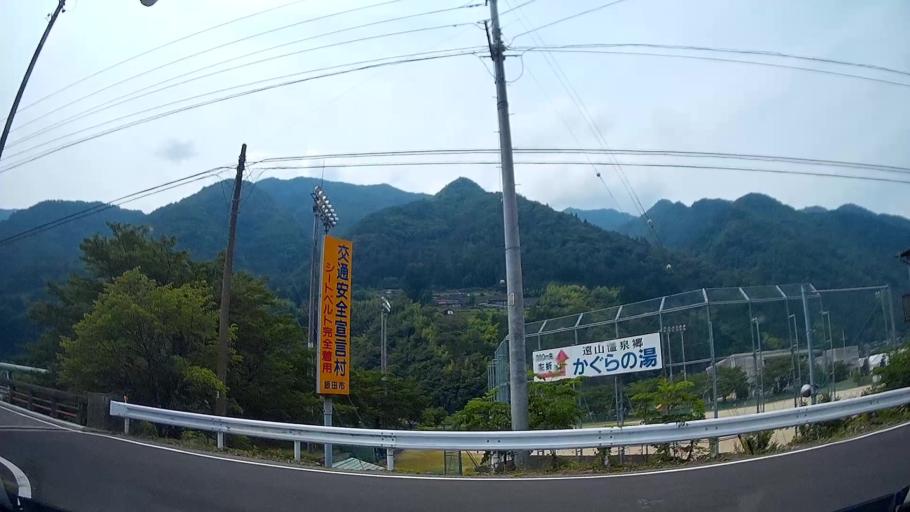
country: JP
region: Nagano
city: Iida
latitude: 35.3151
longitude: 137.9245
